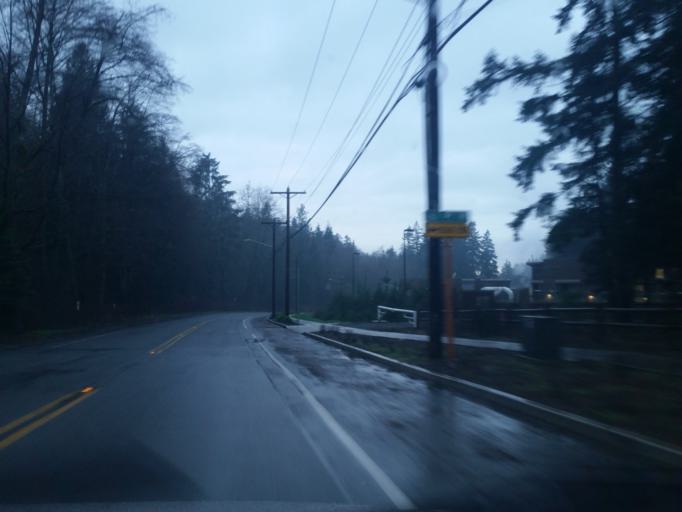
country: US
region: Washington
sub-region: Snohomish County
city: Meadowdale
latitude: 47.8780
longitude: -122.3164
